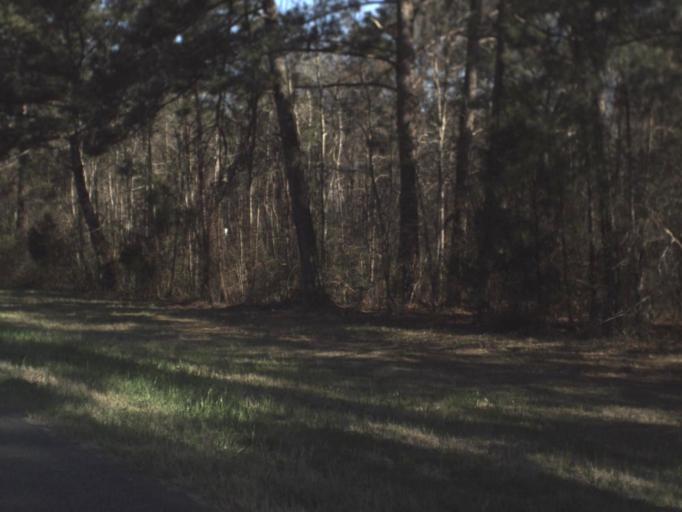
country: US
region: Florida
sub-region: Jackson County
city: Marianna
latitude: 30.7847
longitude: -85.3150
